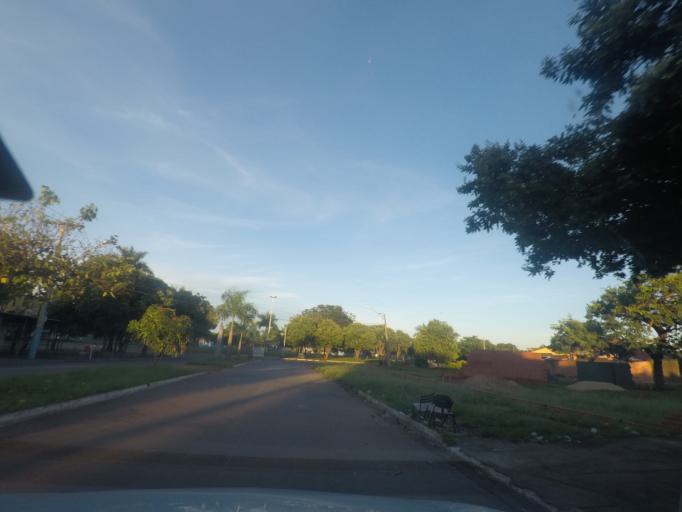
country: BR
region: Goias
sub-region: Goiania
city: Goiania
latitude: -16.6886
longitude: -49.3548
